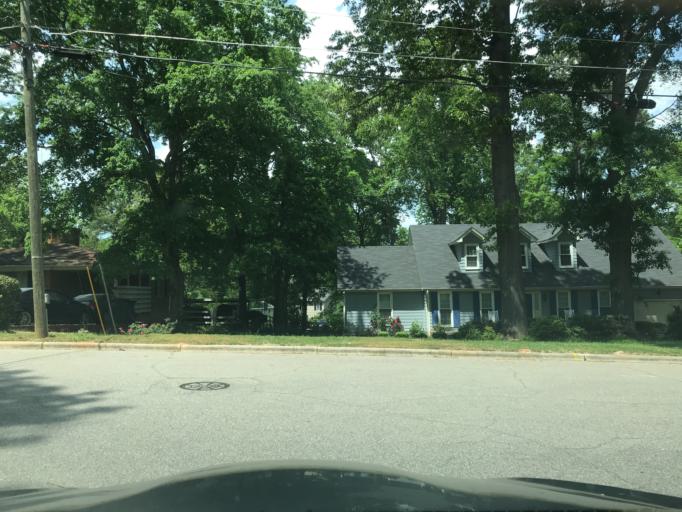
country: US
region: North Carolina
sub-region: Wake County
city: Raleigh
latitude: 35.7761
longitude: -78.6158
